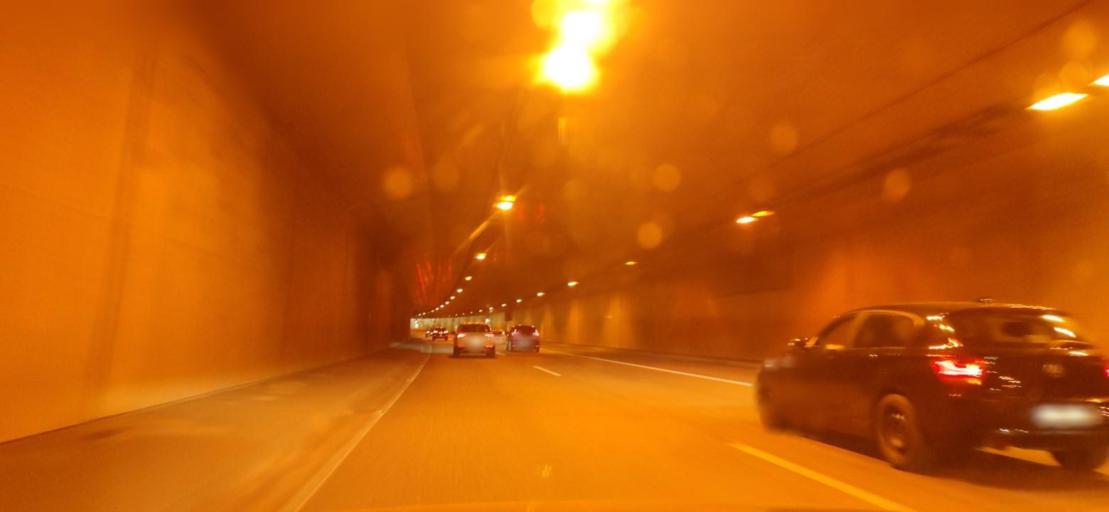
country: DE
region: North Rhine-Westphalia
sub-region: Regierungsbezirk Dusseldorf
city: Ratingen
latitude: 51.2734
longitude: 6.8298
